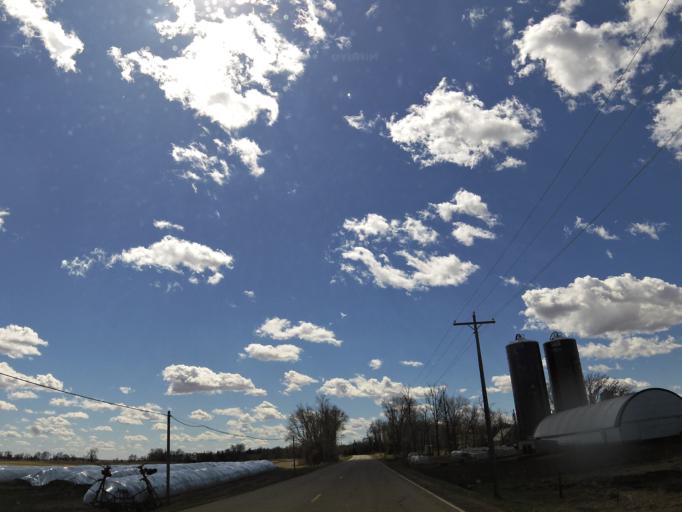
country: US
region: Minnesota
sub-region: Washington County
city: Cottage Grove
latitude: 44.7538
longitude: -92.9307
